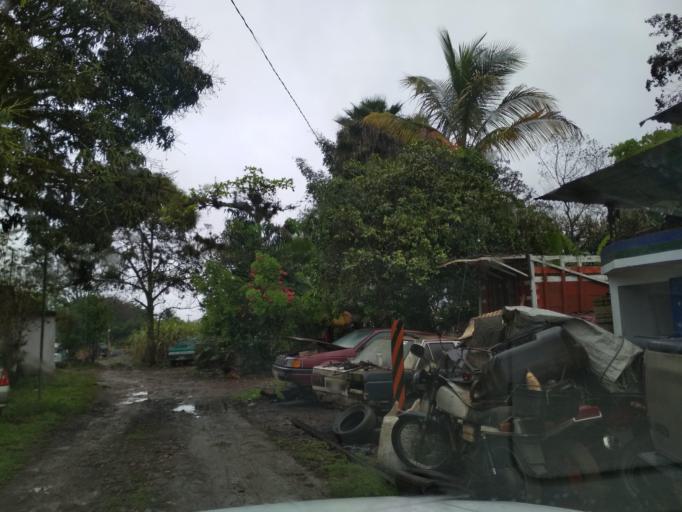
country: MX
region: Veracruz
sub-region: Amatlan de los Reyes
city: Centro de Readaptacion Social
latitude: 18.8317
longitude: -96.9309
